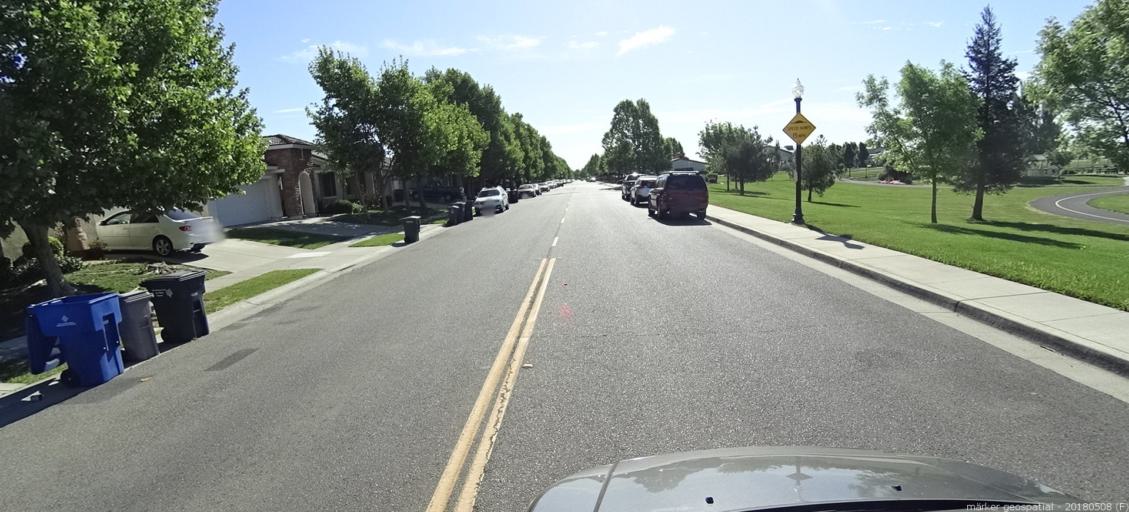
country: US
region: California
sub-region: Sacramento County
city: Elverta
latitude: 38.6820
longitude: -121.5030
